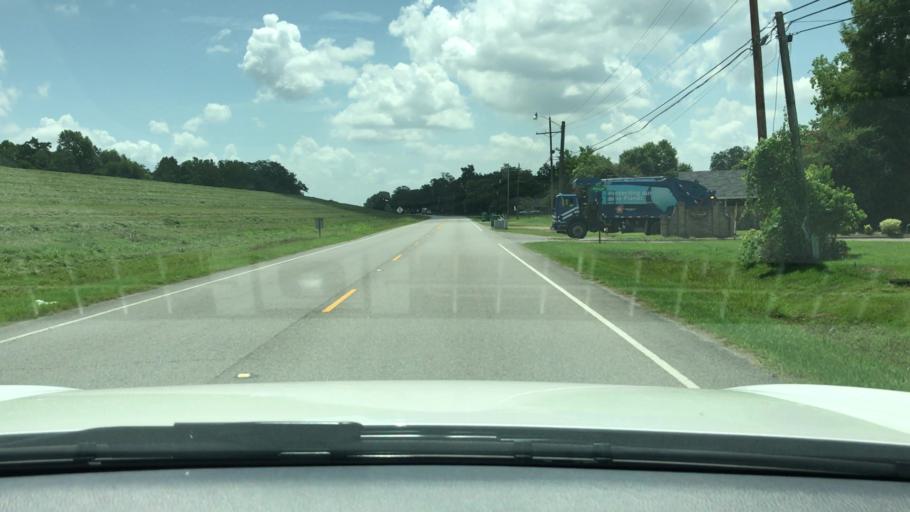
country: US
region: Louisiana
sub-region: Iberville Parish
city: Plaquemine
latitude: 30.2796
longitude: -91.2196
